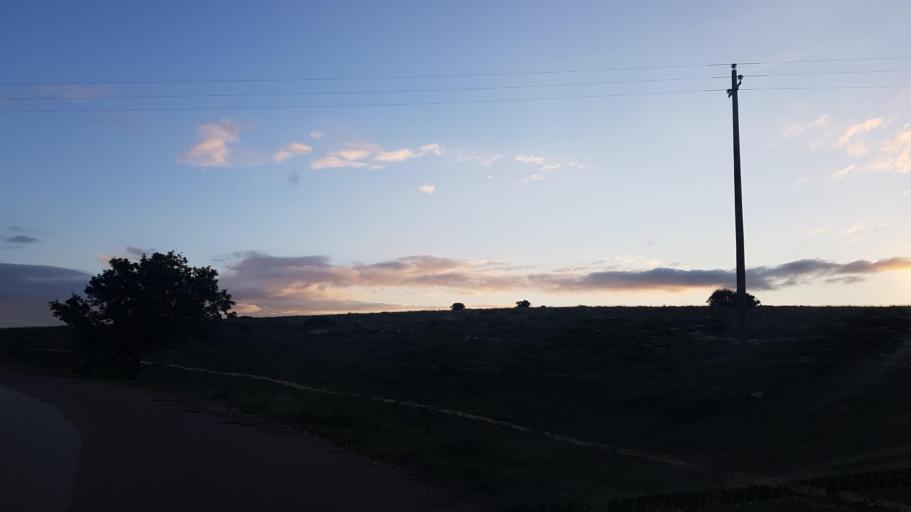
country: IT
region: Basilicate
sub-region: Provincia di Matera
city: Matera
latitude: 40.6743
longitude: 16.6276
